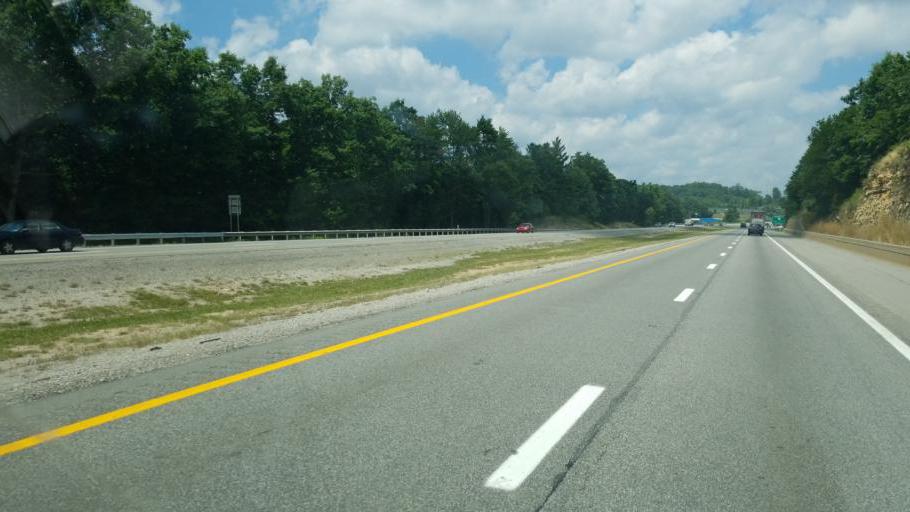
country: US
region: West Virginia
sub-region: Raleigh County
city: Mabscott
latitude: 37.7830
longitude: -81.2207
